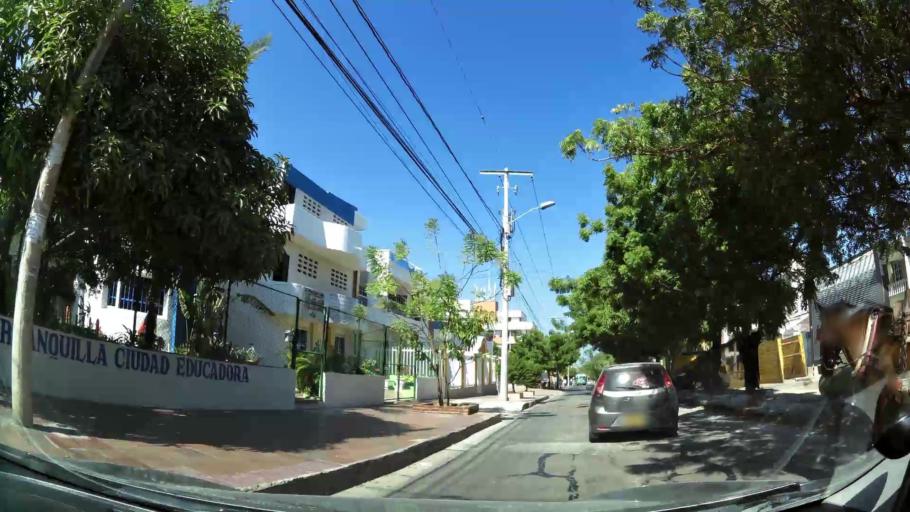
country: CO
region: Atlantico
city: Barranquilla
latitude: 10.9975
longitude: -74.7911
